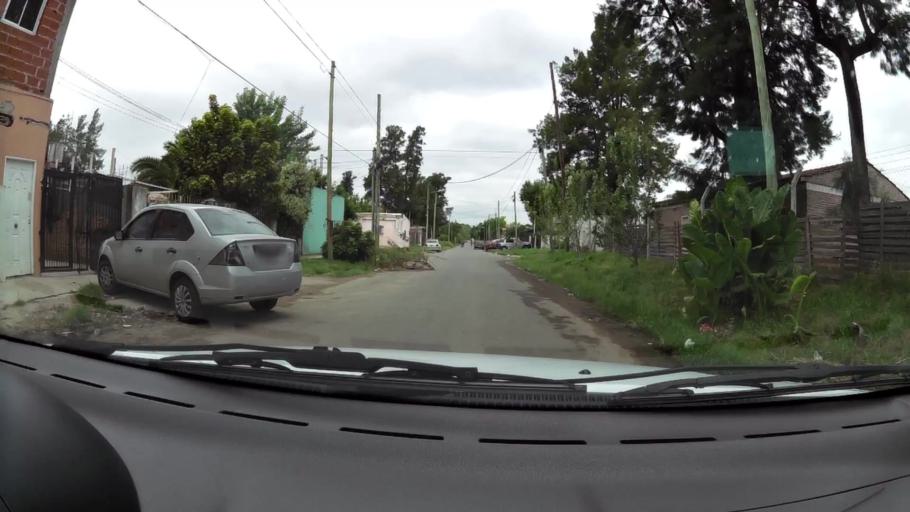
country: AR
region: Buenos Aires
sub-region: Partido de Ezeiza
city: Ezeiza
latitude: -34.8658
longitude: -58.5140
